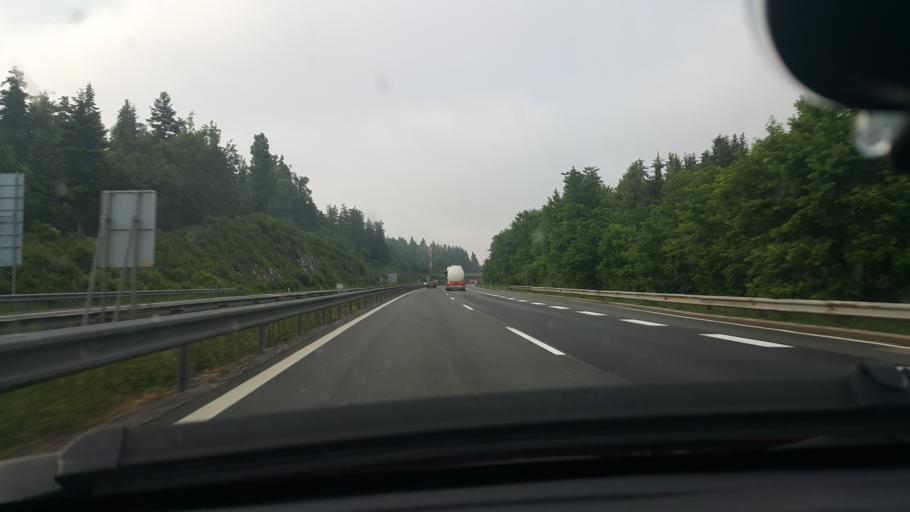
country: SI
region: Logatec
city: Logatec
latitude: 45.9036
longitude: 14.2563
